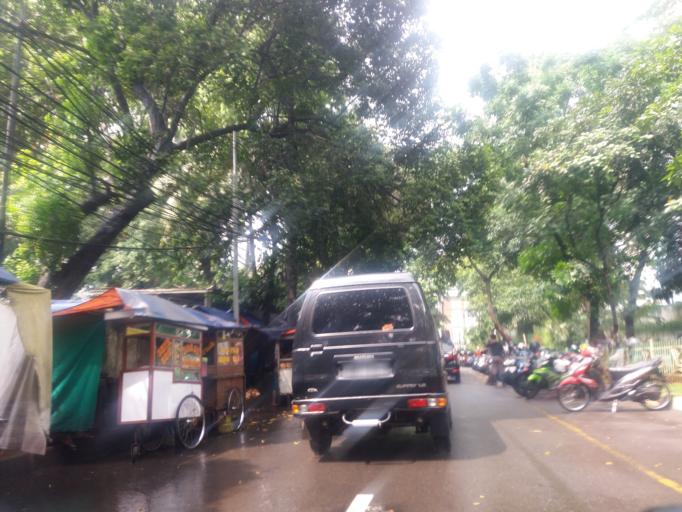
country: ID
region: Jakarta Raya
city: Jakarta
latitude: -6.2150
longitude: 106.8286
